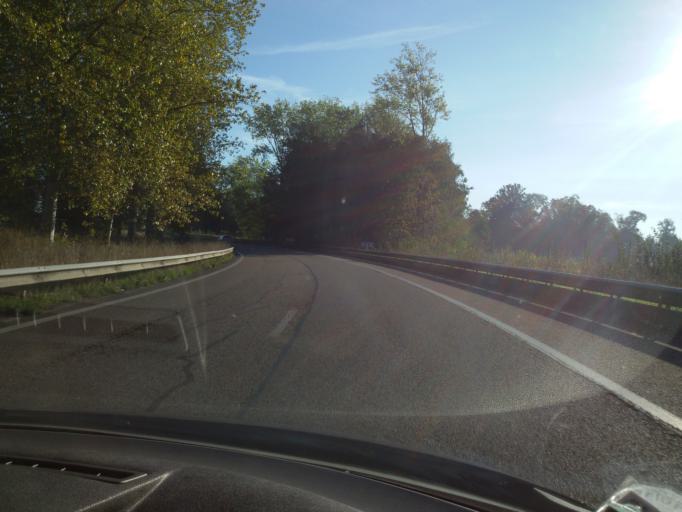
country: FR
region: Ile-de-France
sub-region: Departement de Seine-et-Marne
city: Bailly-Romainvilliers
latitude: 48.8379
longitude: 2.8198
